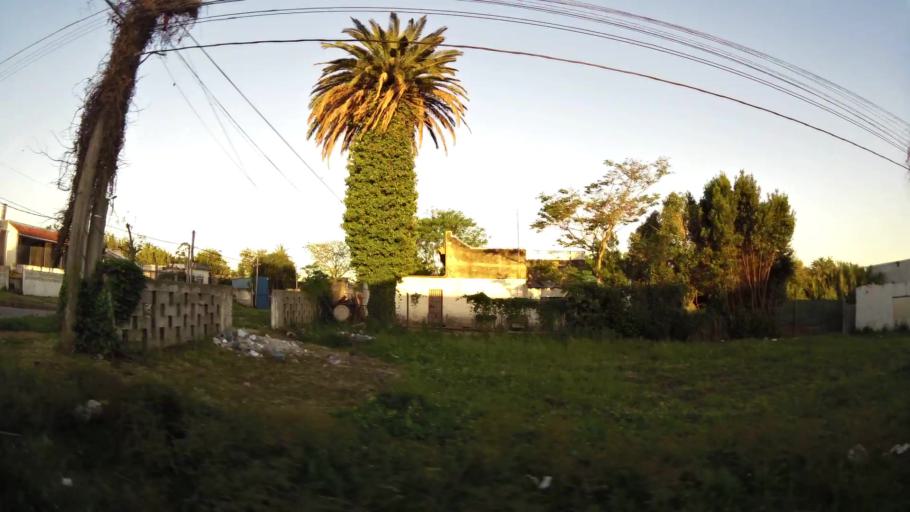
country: UY
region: Montevideo
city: Montevideo
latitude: -34.8308
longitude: -56.1559
